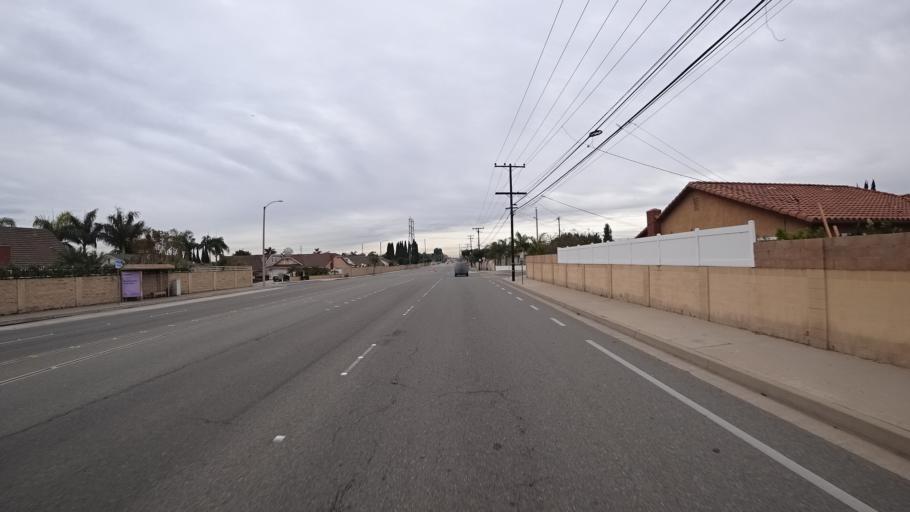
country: US
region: California
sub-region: Orange County
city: Midway City
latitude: 33.7304
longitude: -117.9753
